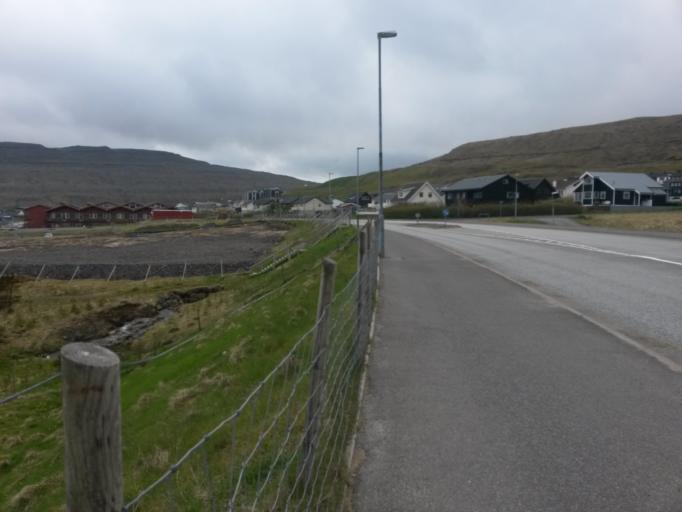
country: FO
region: Streymoy
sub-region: Torshavn
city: Torshavn
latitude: 62.0084
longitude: -6.8003
